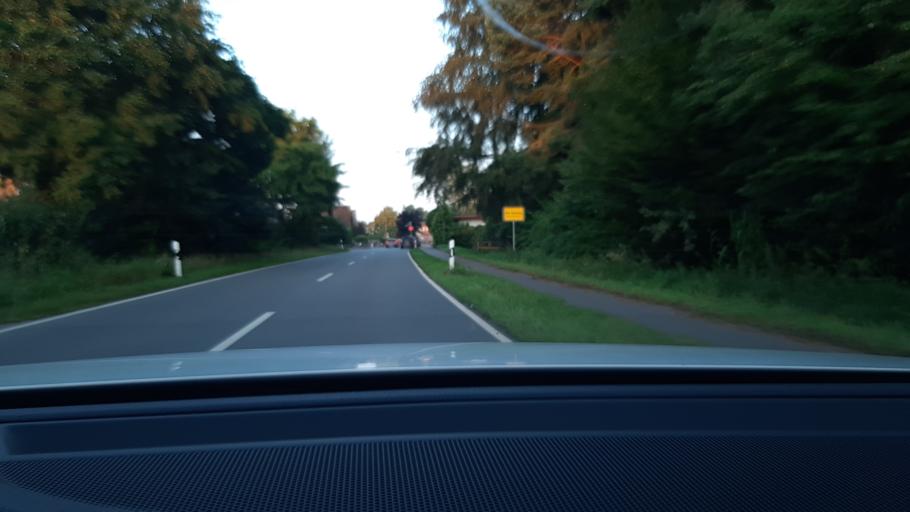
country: DE
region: Schleswig-Holstein
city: Klein Wesenberg
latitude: 53.8155
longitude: 10.5580
